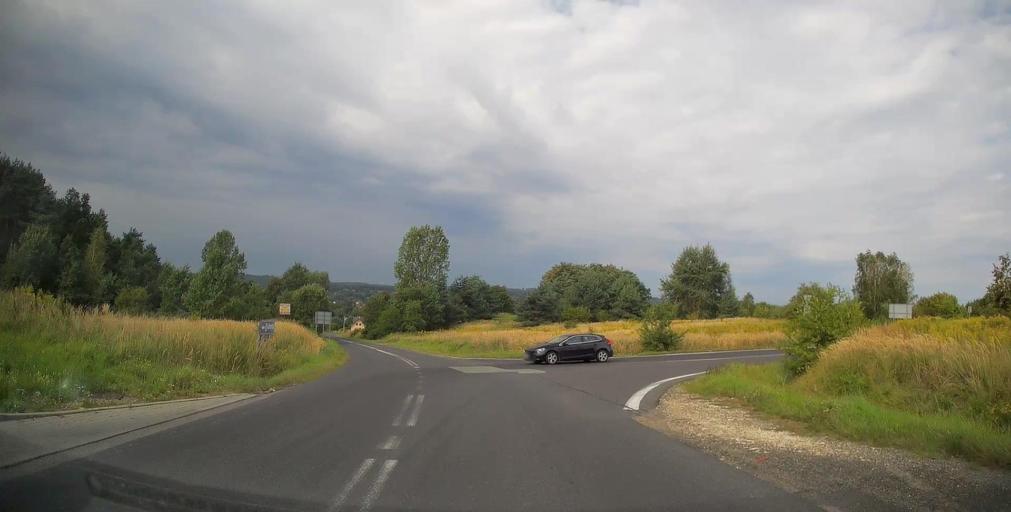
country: PL
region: Lesser Poland Voivodeship
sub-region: Powiat chrzanowski
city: Grojec
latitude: 50.0990
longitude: 19.5493
